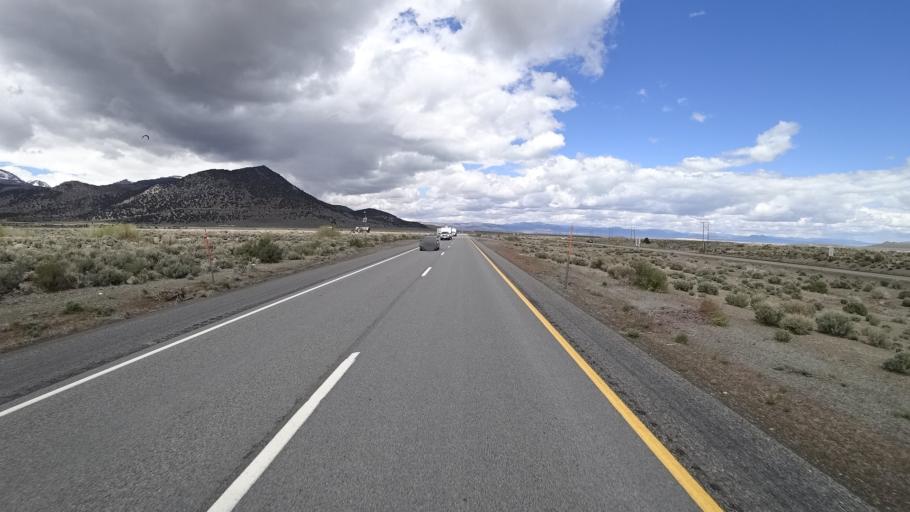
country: US
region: California
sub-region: Mono County
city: Mammoth Lakes
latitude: 37.8980
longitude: -119.0935
